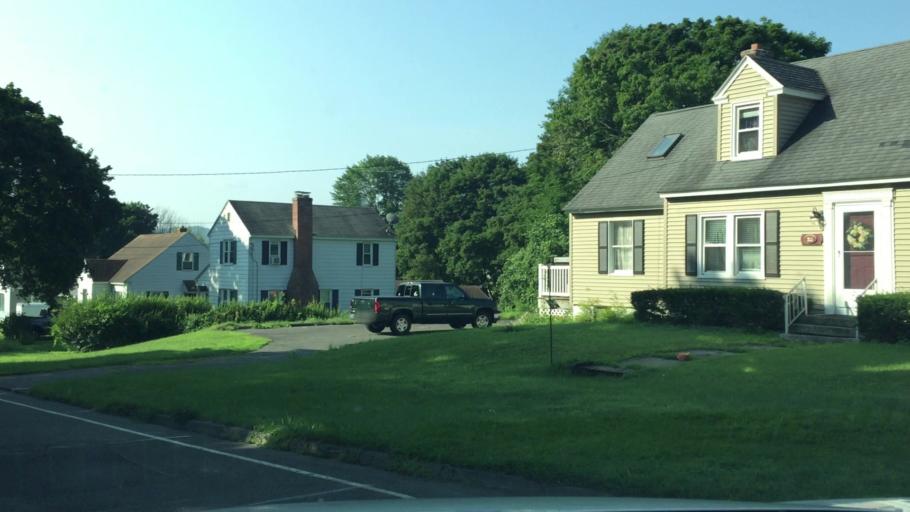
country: US
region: Massachusetts
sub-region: Berkshire County
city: Pittsfield
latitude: 42.4582
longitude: -73.2242
